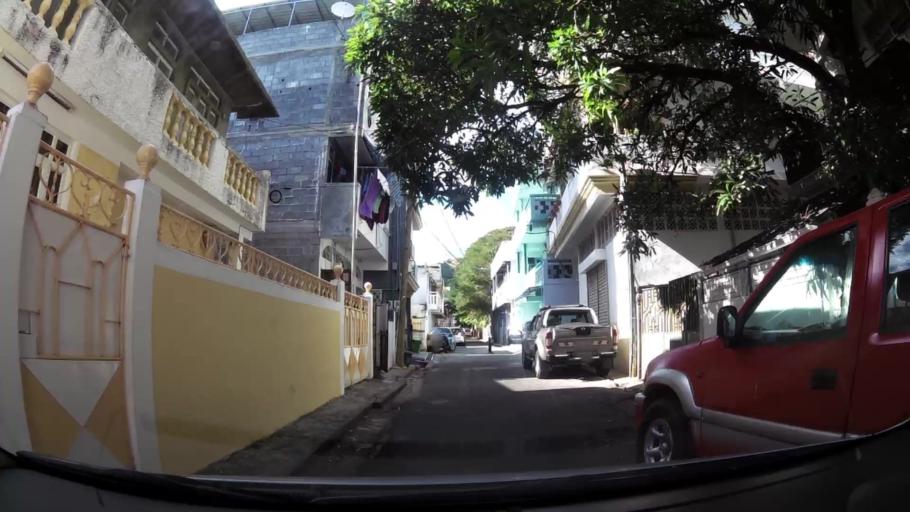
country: MU
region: Pamplemousses
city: Le Hochet
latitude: -20.1531
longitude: 57.5158
